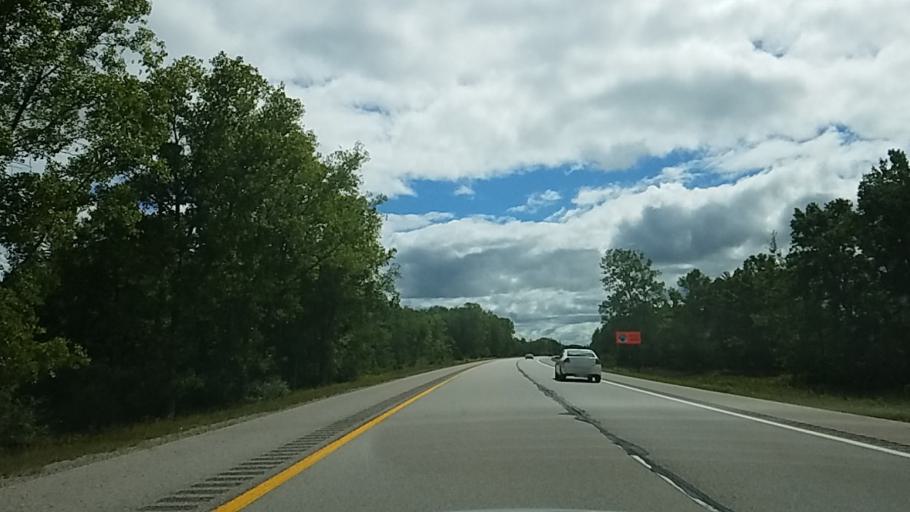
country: US
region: Michigan
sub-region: Ogemaw County
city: Skidway Lake
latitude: 44.0567
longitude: -84.0785
